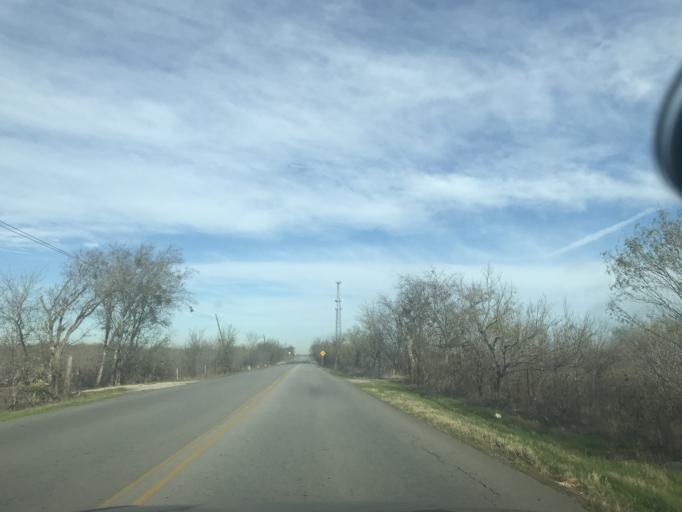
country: US
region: Texas
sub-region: Travis County
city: Manor
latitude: 30.3274
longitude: -97.5460
